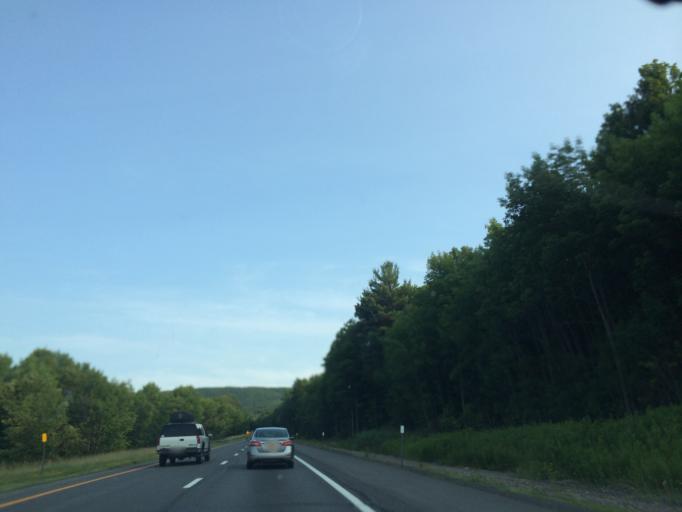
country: US
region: Massachusetts
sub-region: Berkshire County
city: Richmond
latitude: 42.3805
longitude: -73.4648
